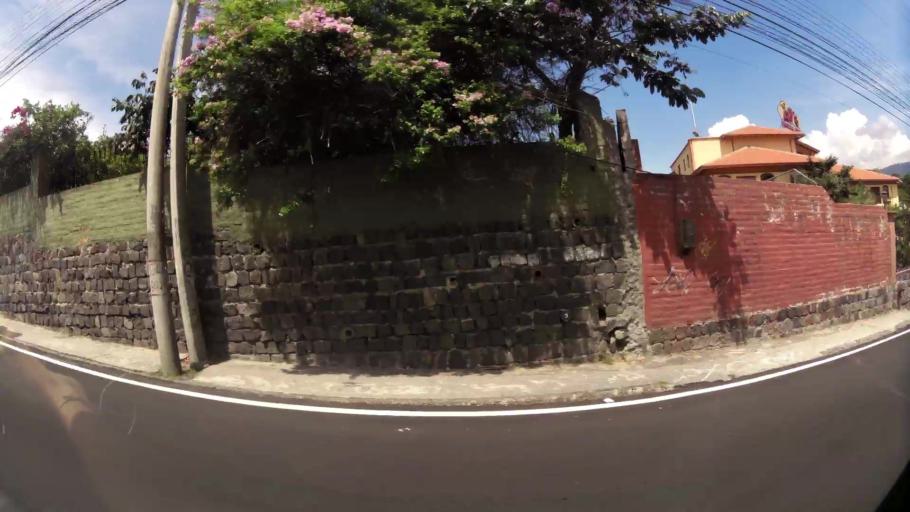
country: EC
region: Pichincha
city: Quito
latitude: -0.2103
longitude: -78.4162
